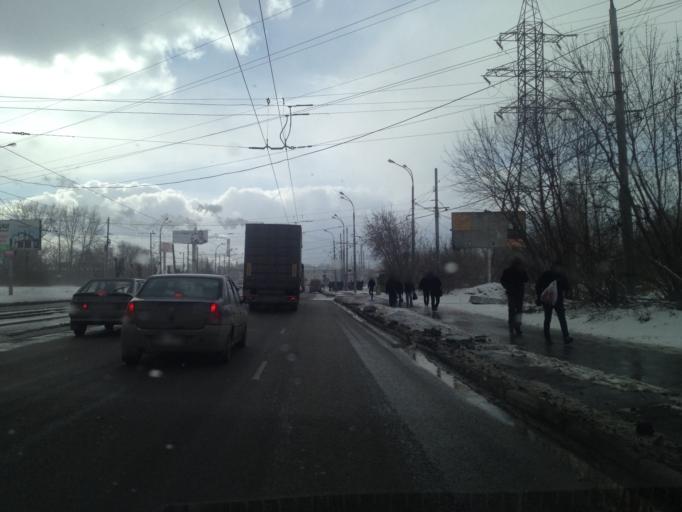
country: RU
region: Sverdlovsk
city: Yekaterinburg
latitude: 56.8782
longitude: 60.6162
